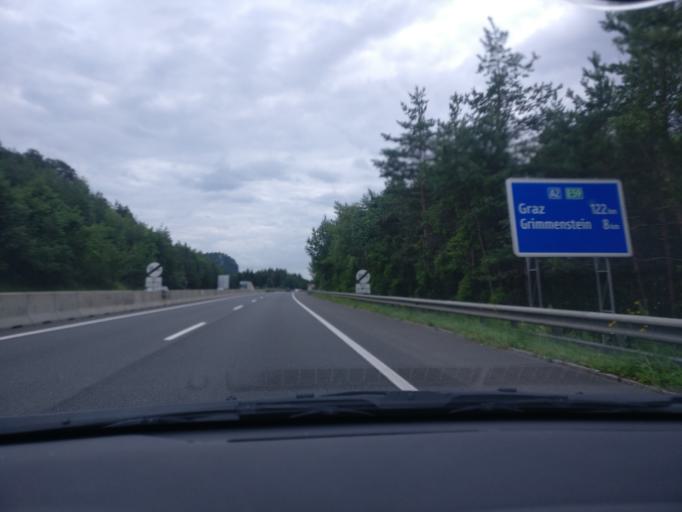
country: AT
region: Lower Austria
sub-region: Politischer Bezirk Neunkirchen
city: Seebenstein
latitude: 47.7009
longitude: 16.1299
